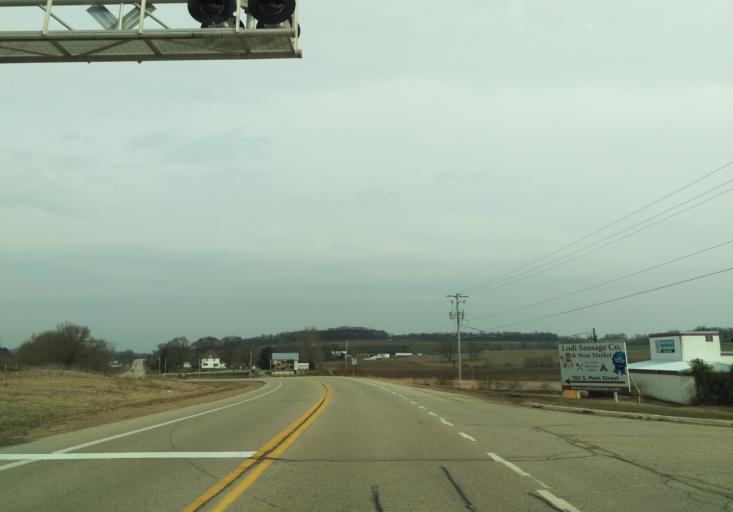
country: US
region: Wisconsin
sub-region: Columbia County
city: Lodi
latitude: 43.2937
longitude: -89.5218
